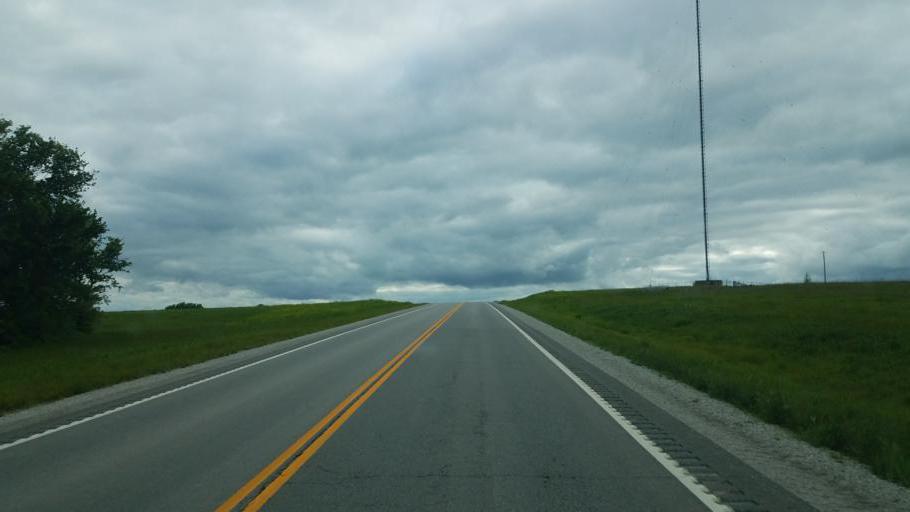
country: US
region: Missouri
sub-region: Harrison County
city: Bethany
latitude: 40.3206
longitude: -93.8020
